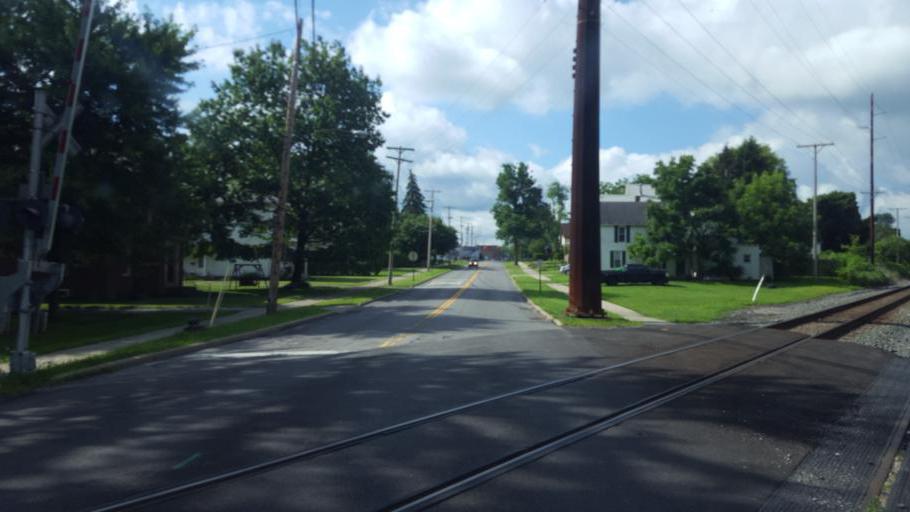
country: US
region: Ohio
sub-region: Richland County
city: Shelby
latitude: 40.8851
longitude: -82.6620
